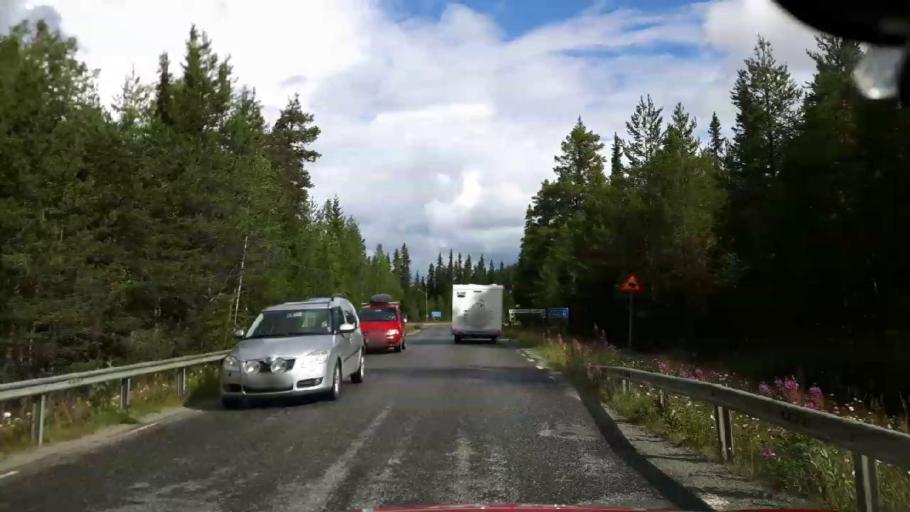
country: SE
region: Vaesterbotten
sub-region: Vilhelmina Kommun
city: Sjoberg
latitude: 64.9369
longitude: 15.8583
